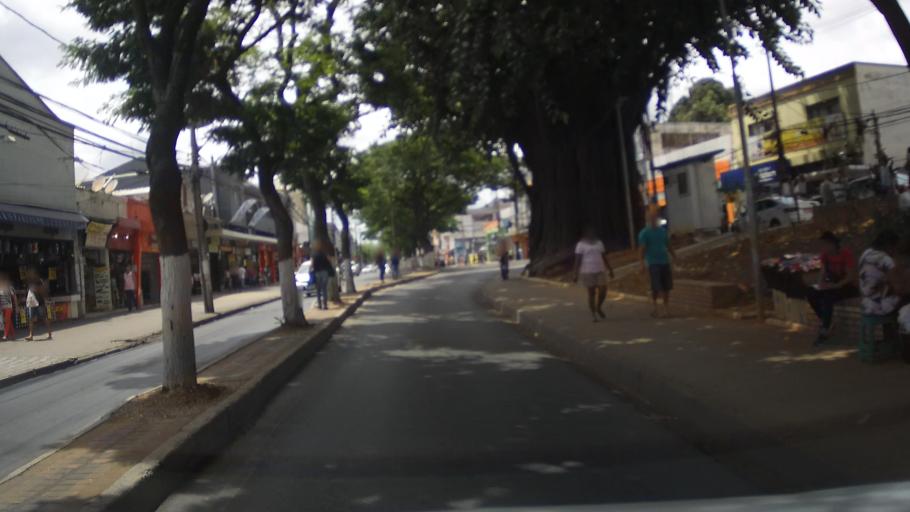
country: BR
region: Minas Gerais
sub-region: Belo Horizonte
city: Belo Horizonte
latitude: -19.8147
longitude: -43.9597
